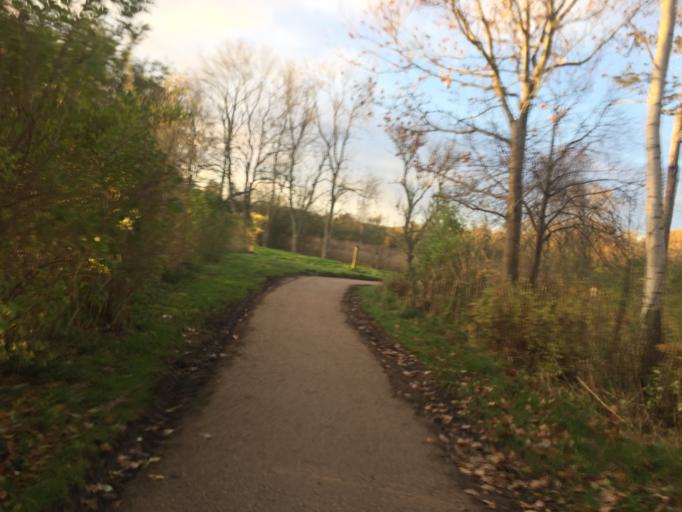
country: DK
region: Zealand
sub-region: Ringsted Kommune
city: Ringsted
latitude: 55.4207
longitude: 11.7802
